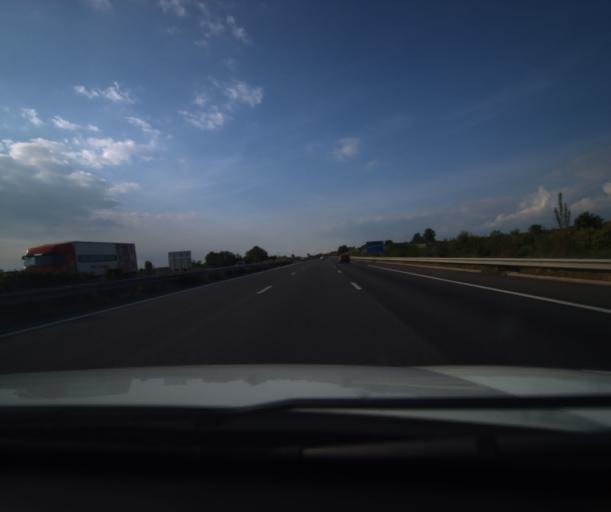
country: FR
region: Midi-Pyrenees
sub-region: Departement de la Haute-Garonne
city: Bouloc
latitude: 43.7786
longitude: 1.3834
